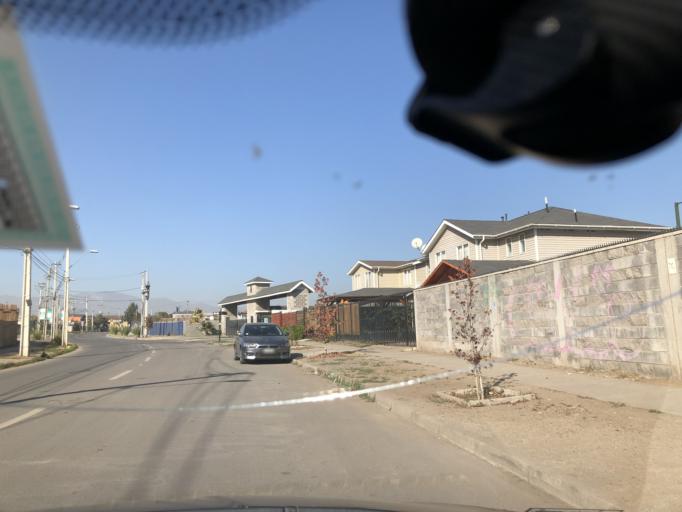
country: CL
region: Santiago Metropolitan
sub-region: Provincia de Cordillera
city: Puente Alto
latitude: -33.5763
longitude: -70.5937
